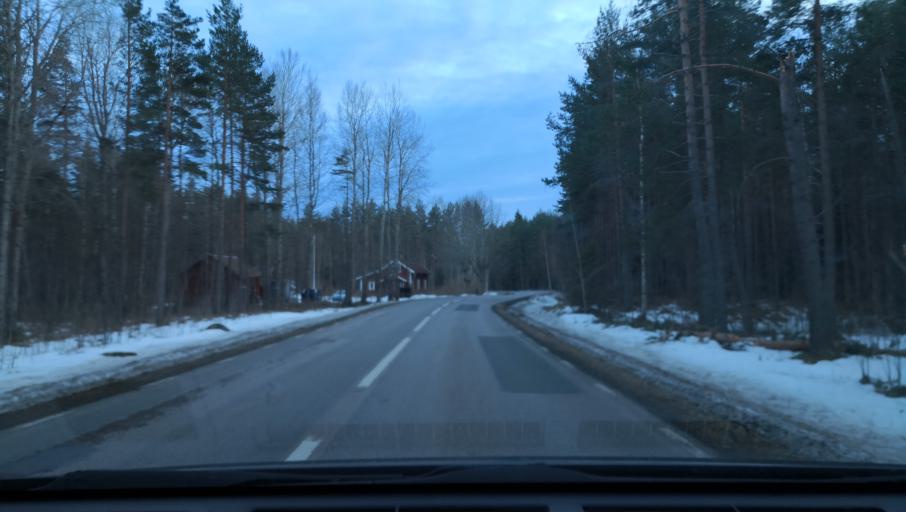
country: SE
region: Uppsala
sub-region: Osthammars Kommun
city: Osterbybruk
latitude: 60.2703
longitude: 17.9569
